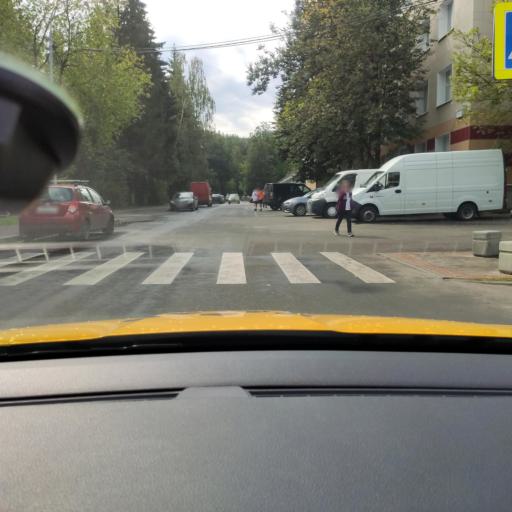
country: RU
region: Moskovskaya
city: Troitsk
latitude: 55.4730
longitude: 37.3009
